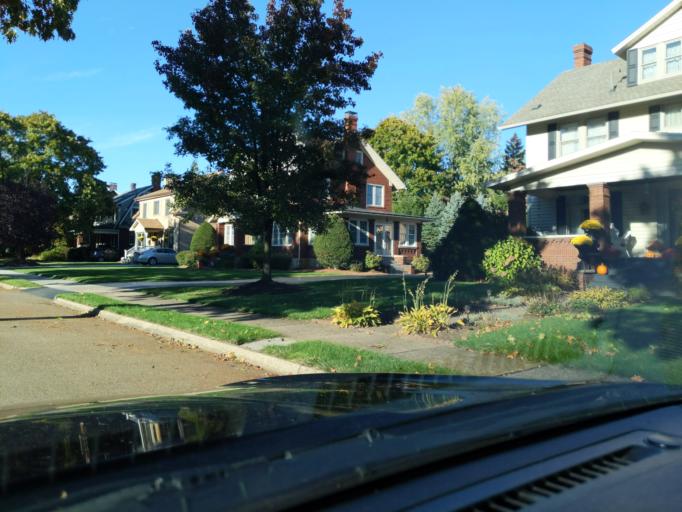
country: US
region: Pennsylvania
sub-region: Blair County
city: Lakemont
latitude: 40.4850
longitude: -78.4061
